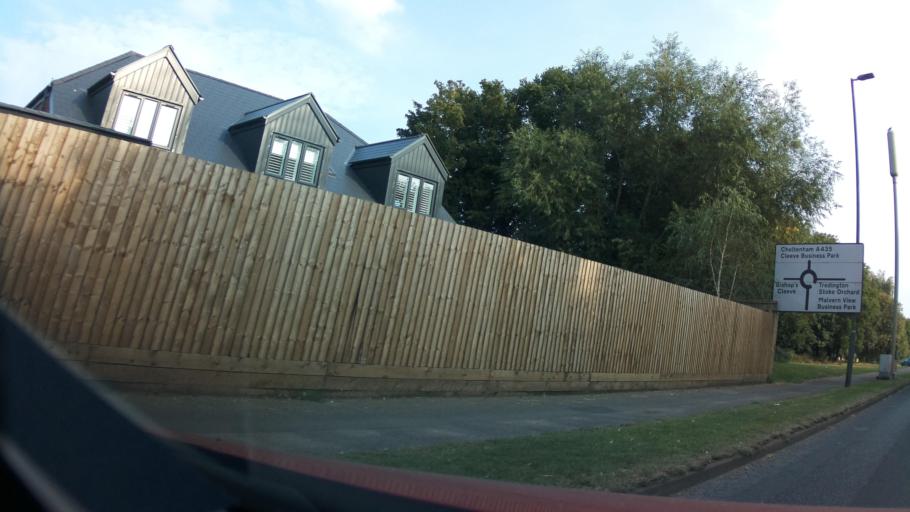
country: GB
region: England
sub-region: Gloucestershire
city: Gotherington
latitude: 51.9471
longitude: -2.0725
